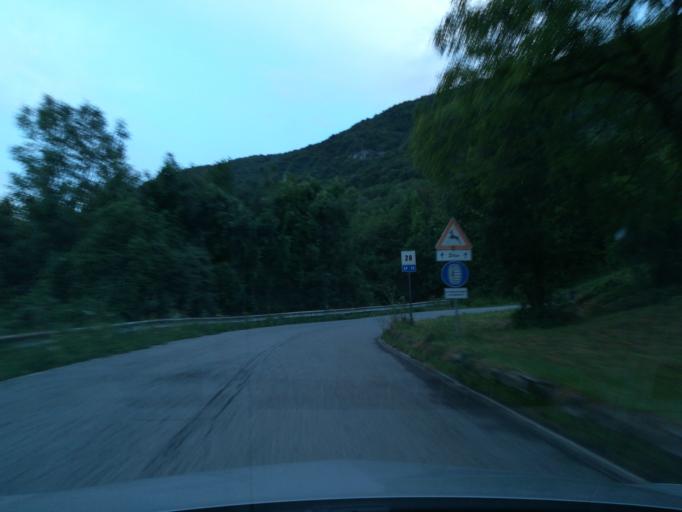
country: IT
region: Lombardy
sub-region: Provincia di Bergamo
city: Valsecca
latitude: 45.8205
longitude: 9.4877
